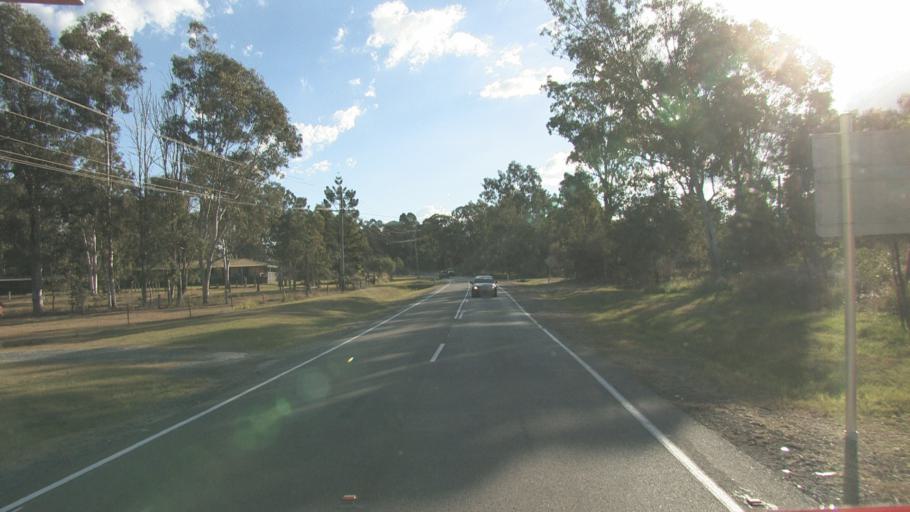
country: AU
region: Queensland
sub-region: Logan
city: Park Ridge South
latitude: -27.7172
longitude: 152.9740
